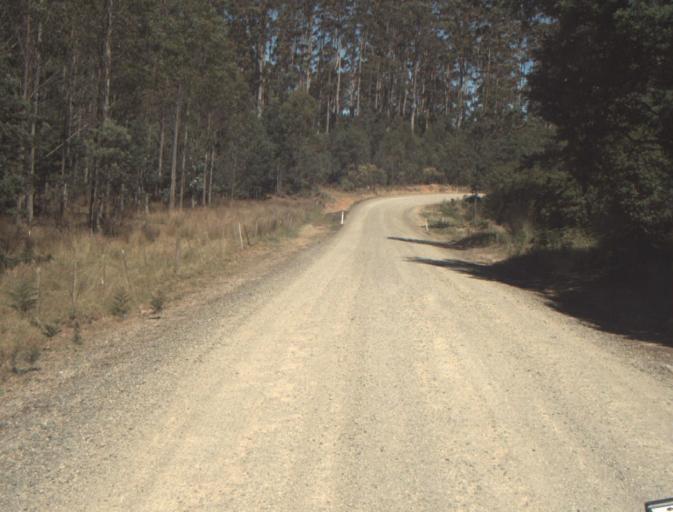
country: AU
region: Tasmania
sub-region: Dorset
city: Scottsdale
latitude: -41.3350
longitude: 147.4338
